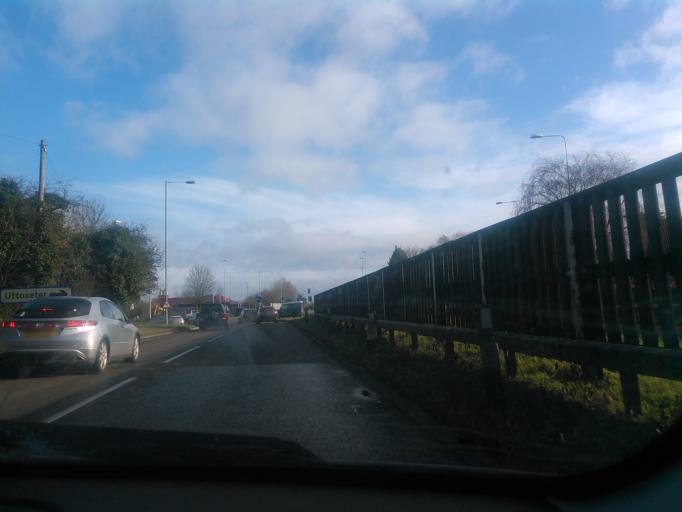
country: GB
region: England
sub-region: Staffordshire
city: Uttoxeter
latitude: 52.9099
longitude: -1.8737
